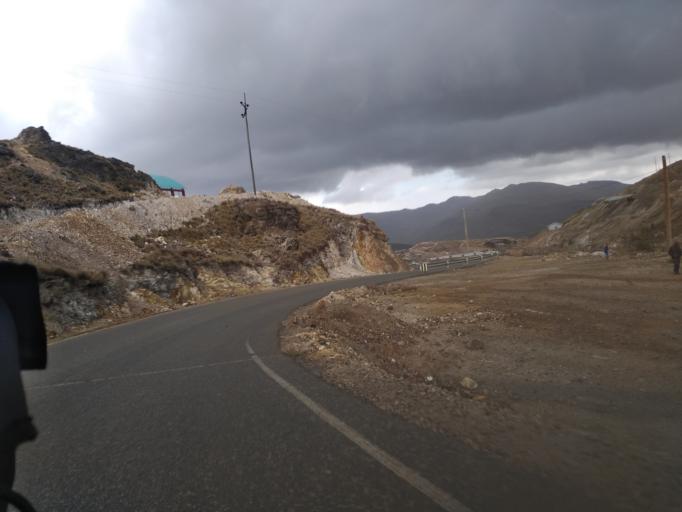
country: PE
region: La Libertad
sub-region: Provincia de Santiago de Chuco
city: Quiruvilca
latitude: -7.9987
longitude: -78.3082
